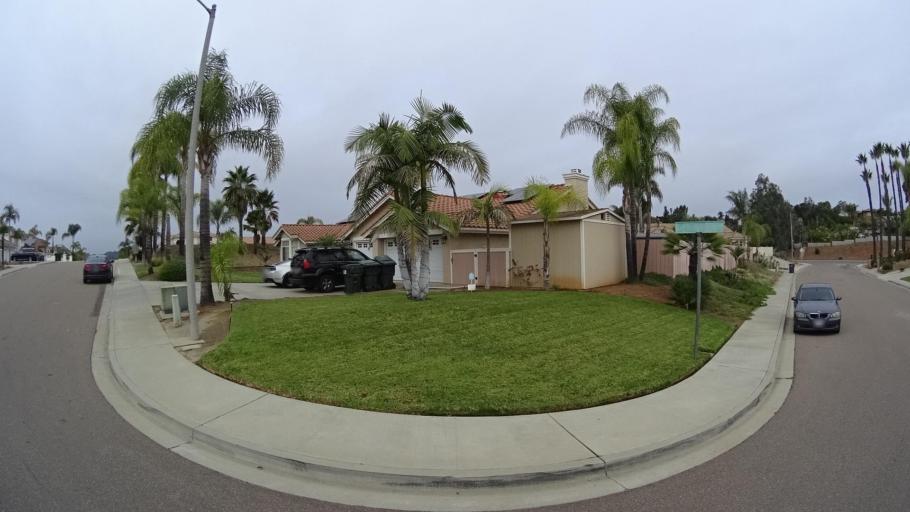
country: US
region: California
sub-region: San Diego County
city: Rancho San Diego
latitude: 32.7611
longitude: -116.9114
